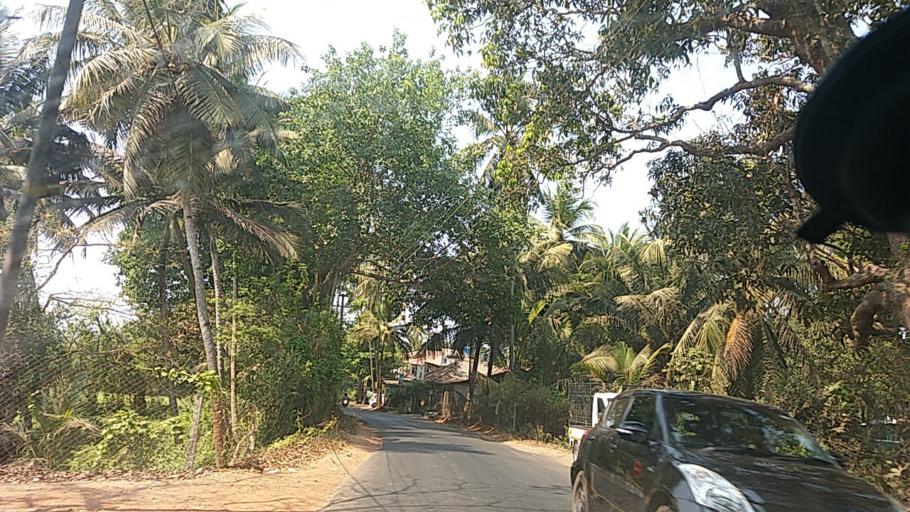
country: IN
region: Goa
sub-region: North Goa
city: Saligao
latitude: 15.5424
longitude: 73.7896
